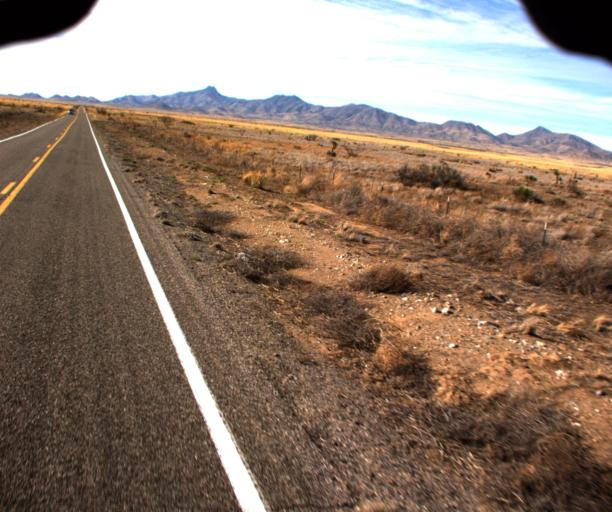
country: US
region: Arizona
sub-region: Cochise County
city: Willcox
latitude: 32.0723
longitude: -109.5131
